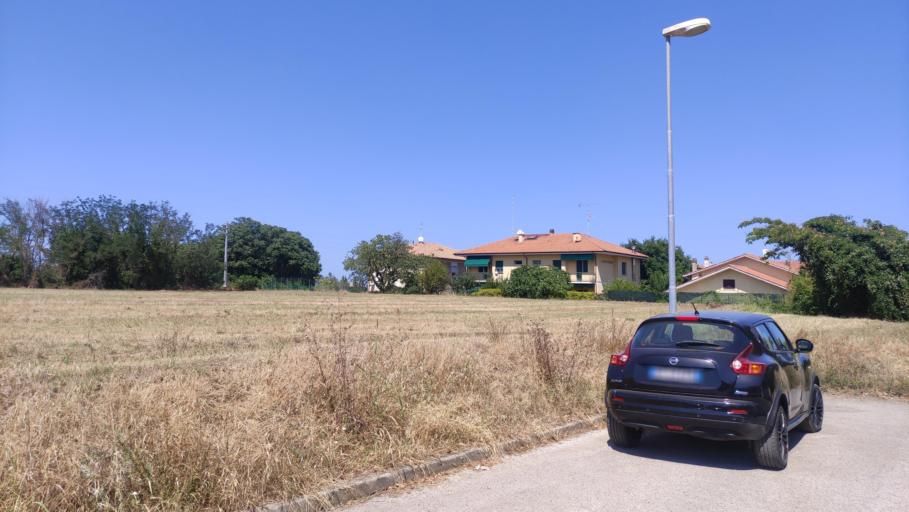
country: IT
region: The Marches
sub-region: Provincia di Pesaro e Urbino
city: Fano
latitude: 43.8490
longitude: 13.0041
